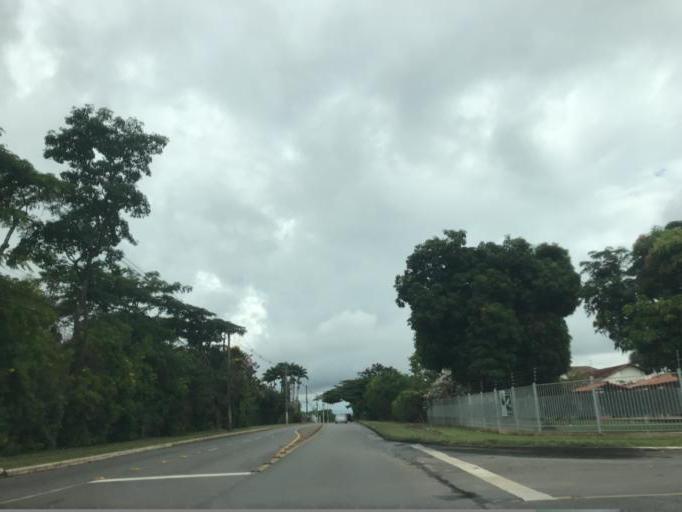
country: BR
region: Federal District
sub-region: Brasilia
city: Brasilia
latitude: -15.8508
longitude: -47.8819
